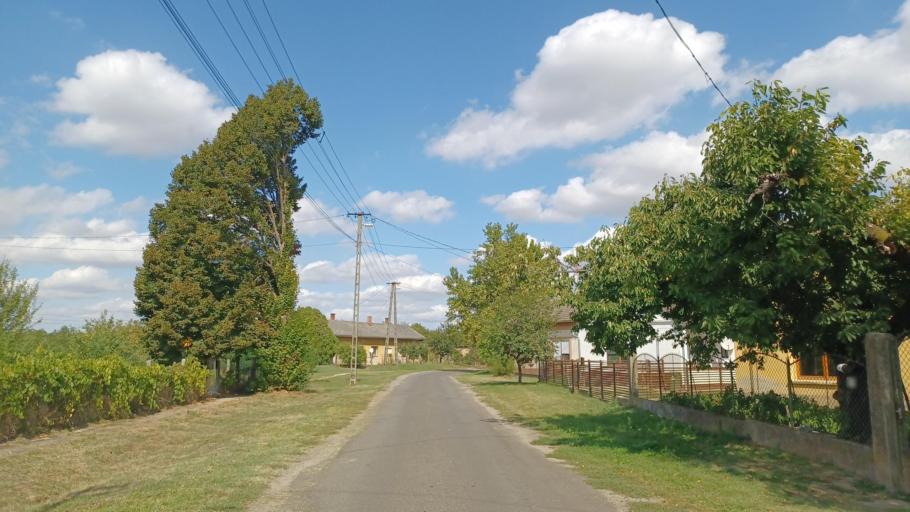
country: HU
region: Tolna
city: Pincehely
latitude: 46.7257
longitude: 18.4750
